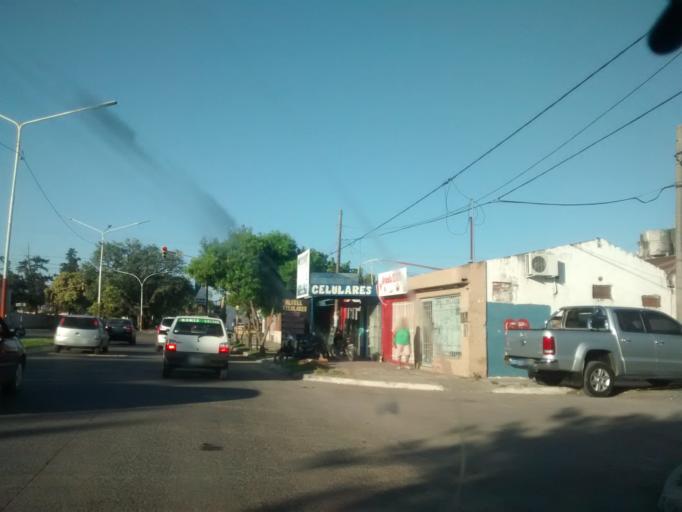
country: AR
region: Chaco
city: Resistencia
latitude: -27.4581
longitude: -59.0084
